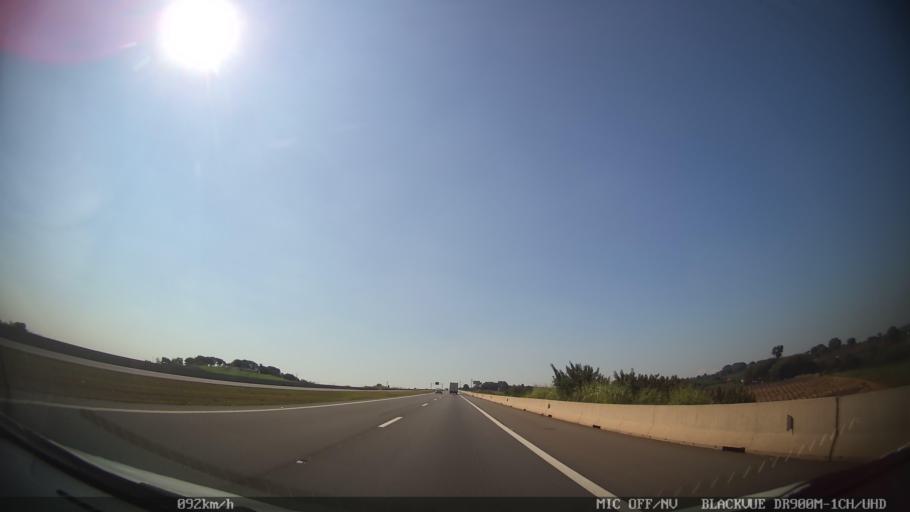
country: BR
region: Sao Paulo
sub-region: Valinhos
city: Valinhos
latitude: -22.9995
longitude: -47.0776
